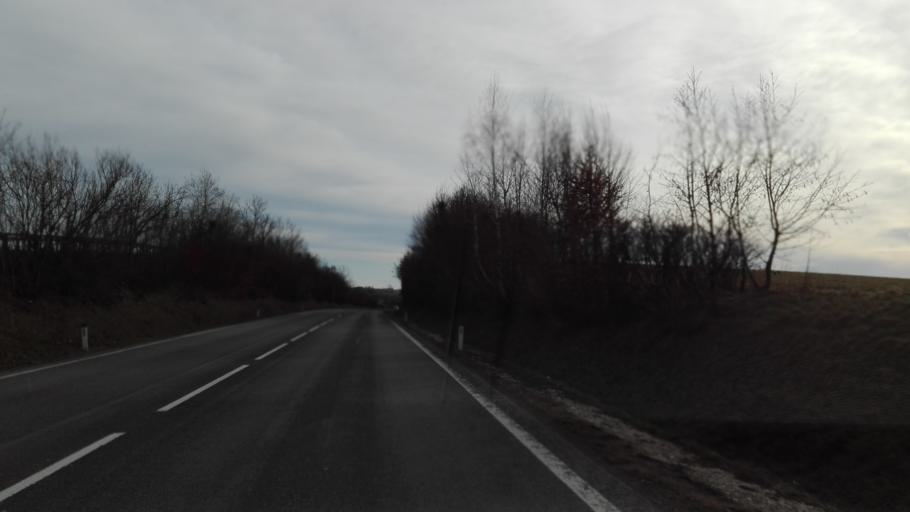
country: AT
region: Upper Austria
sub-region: Politischer Bezirk Rohrbach
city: Kleinzell im Muehlkreis
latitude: 48.5161
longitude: 13.9886
